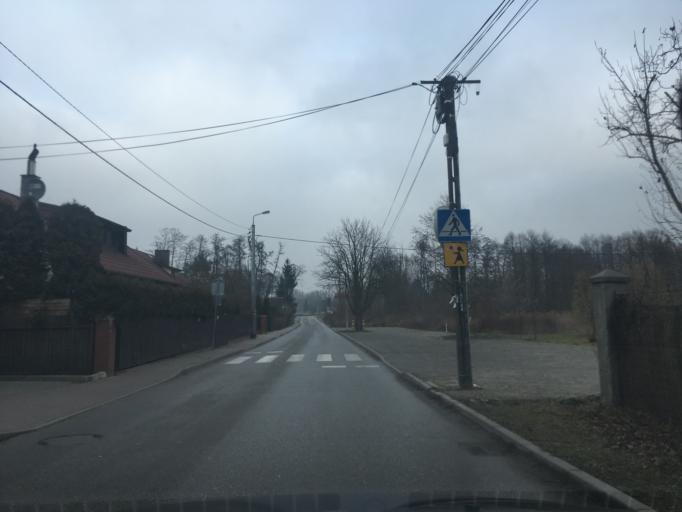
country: PL
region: Masovian Voivodeship
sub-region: Powiat piaseczynski
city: Lesznowola
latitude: 52.0372
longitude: 20.9440
